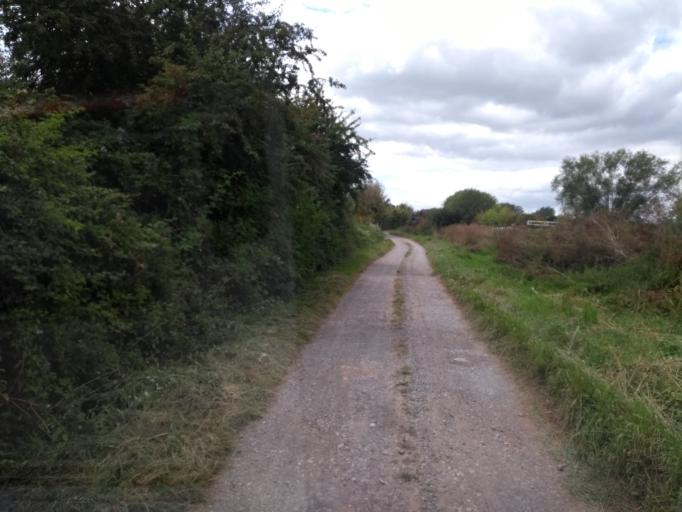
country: GB
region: England
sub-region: Somerset
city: North Petherton
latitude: 51.0777
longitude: -2.9918
